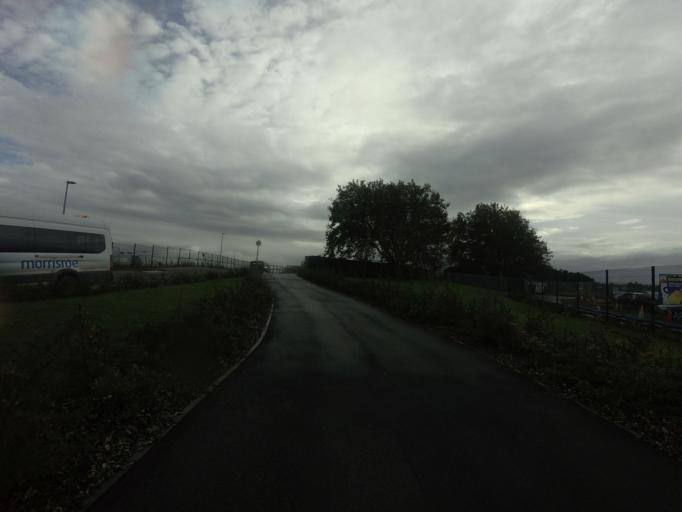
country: GB
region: England
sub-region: Greater London
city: Abbey Wood
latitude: 51.5186
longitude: 0.1148
